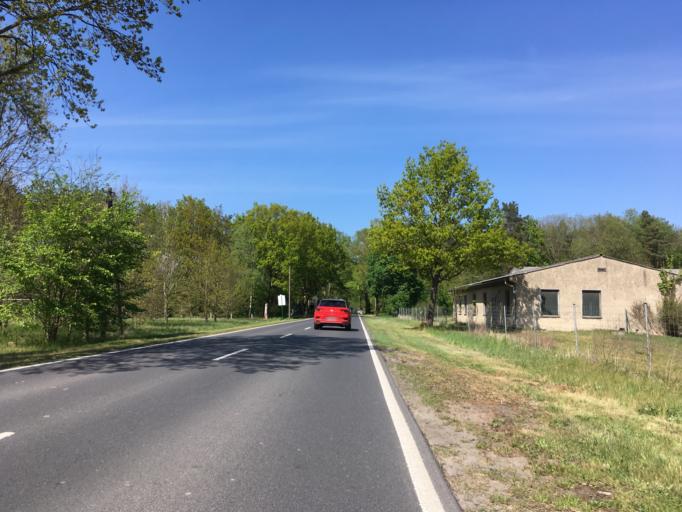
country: DE
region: Brandenburg
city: Rudnitz
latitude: 52.7655
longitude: 13.5654
